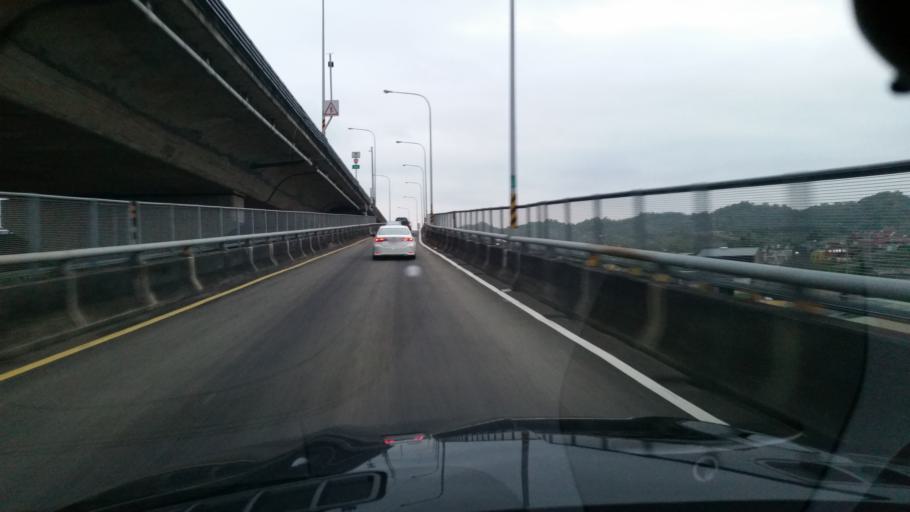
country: TW
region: Taiwan
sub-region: Miaoli
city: Miaoli
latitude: 24.5751
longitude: 120.8466
